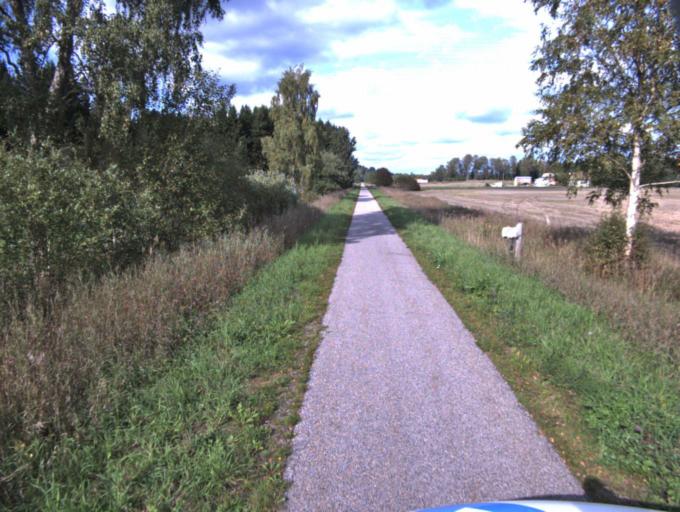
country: SE
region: Vaestra Goetaland
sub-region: Ulricehamns Kommun
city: Ulricehamn
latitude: 57.8786
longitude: 13.4294
